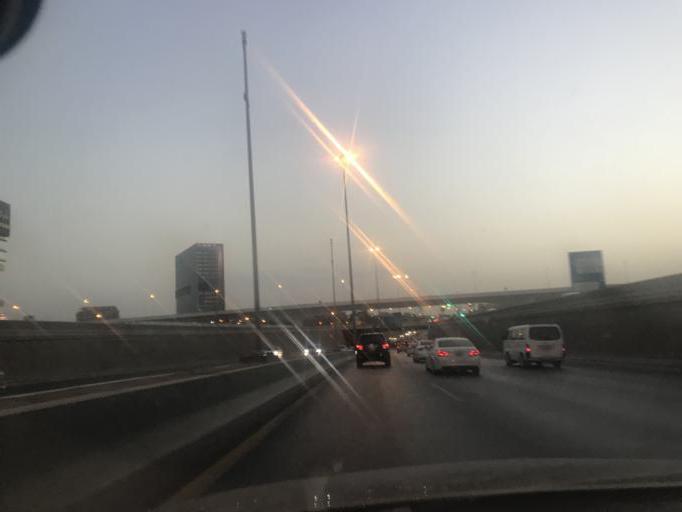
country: SA
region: Ar Riyad
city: Riyadh
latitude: 24.6759
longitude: 46.6809
